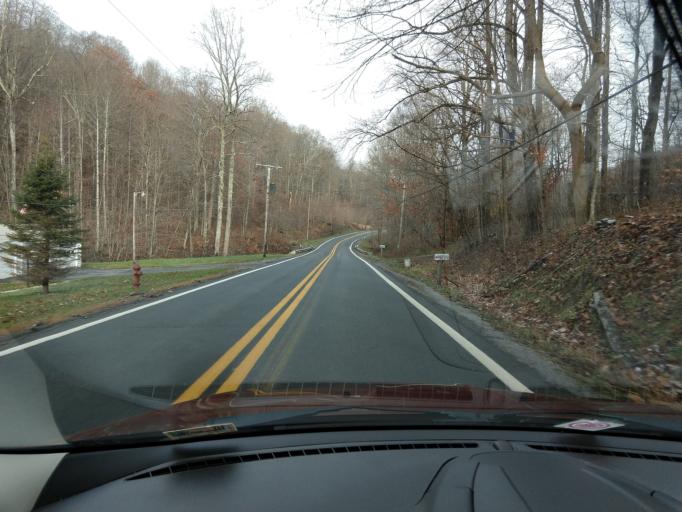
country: US
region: West Virginia
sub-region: Greenbrier County
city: Rainelle
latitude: 38.0766
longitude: -80.7077
